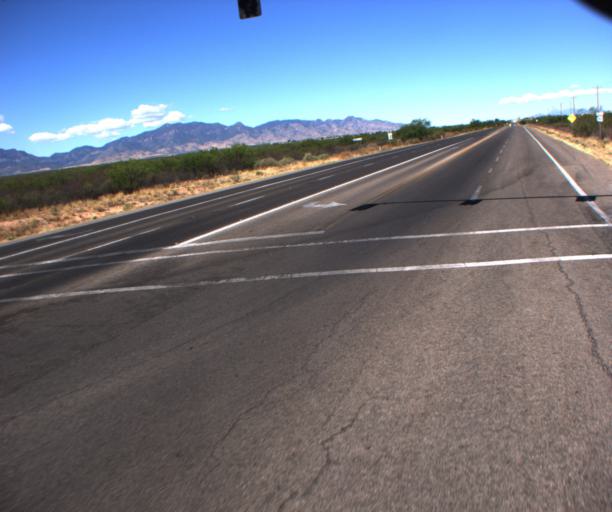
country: US
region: Arizona
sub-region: Cochise County
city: Sierra Vista Southeast
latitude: 31.5518
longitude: -110.1899
